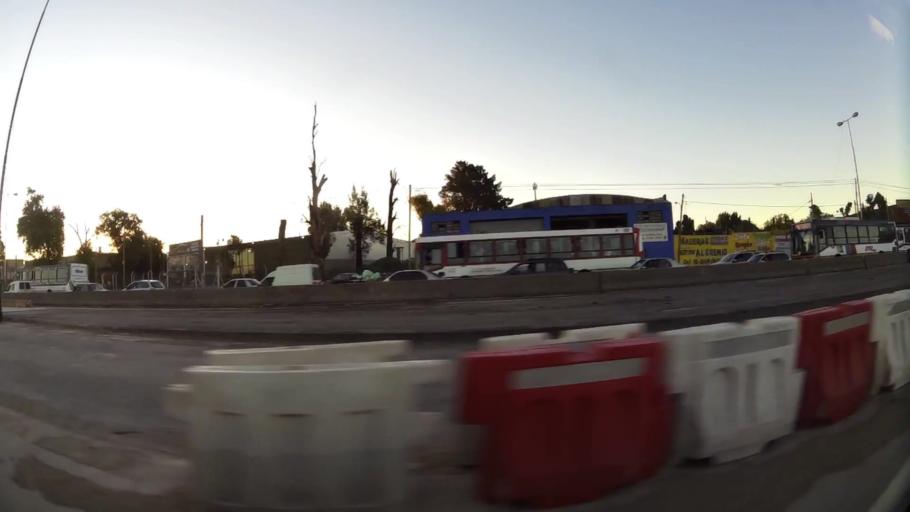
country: AR
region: Buenos Aires
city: Pontevedra
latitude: -34.7526
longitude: -58.6138
